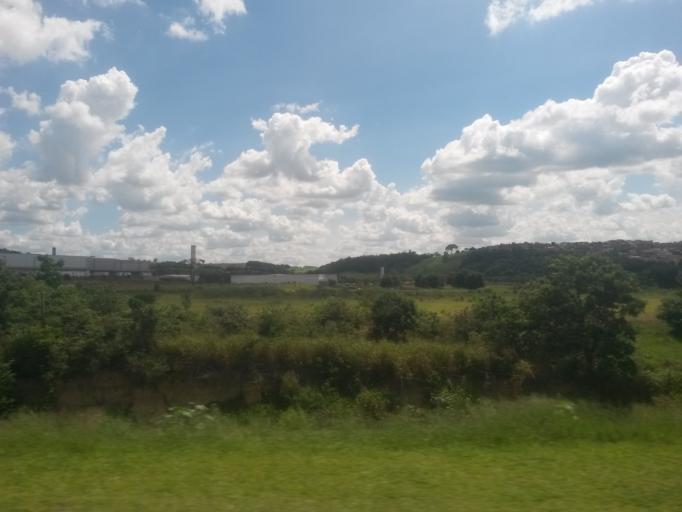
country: BR
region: Sao Paulo
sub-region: Vinhedo
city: Vinhedo
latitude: -23.0532
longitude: -46.9997
